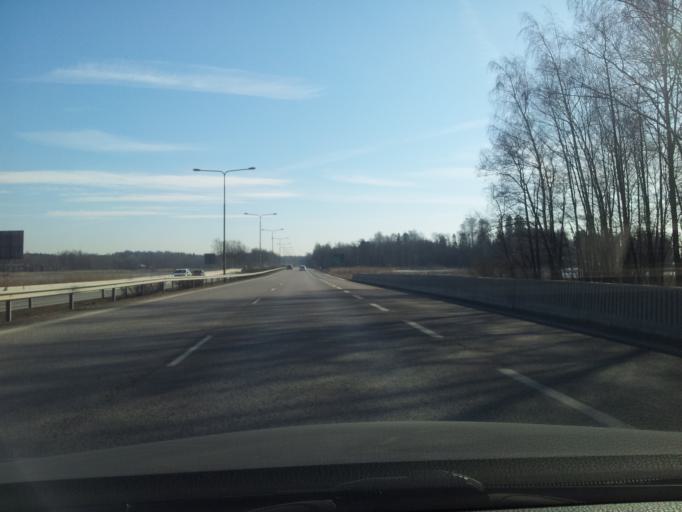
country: FI
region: Uusimaa
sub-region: Helsinki
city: Teekkarikylae
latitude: 60.2064
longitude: 24.8412
